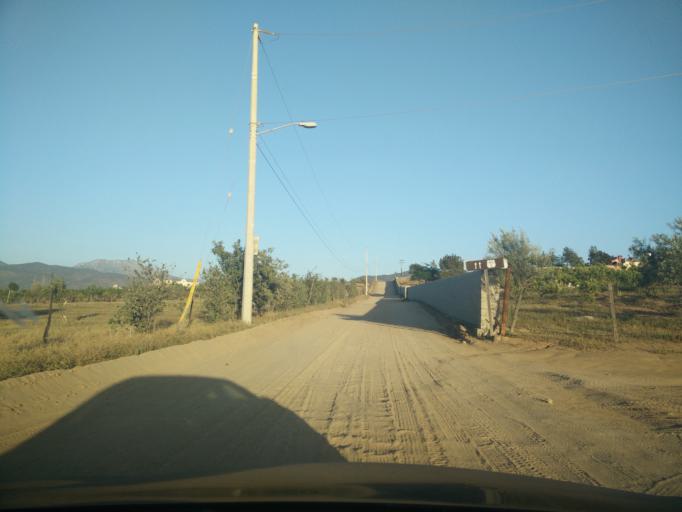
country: MX
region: Baja California
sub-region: Ensenada
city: Rancho Verde
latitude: 32.0444
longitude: -116.6446
